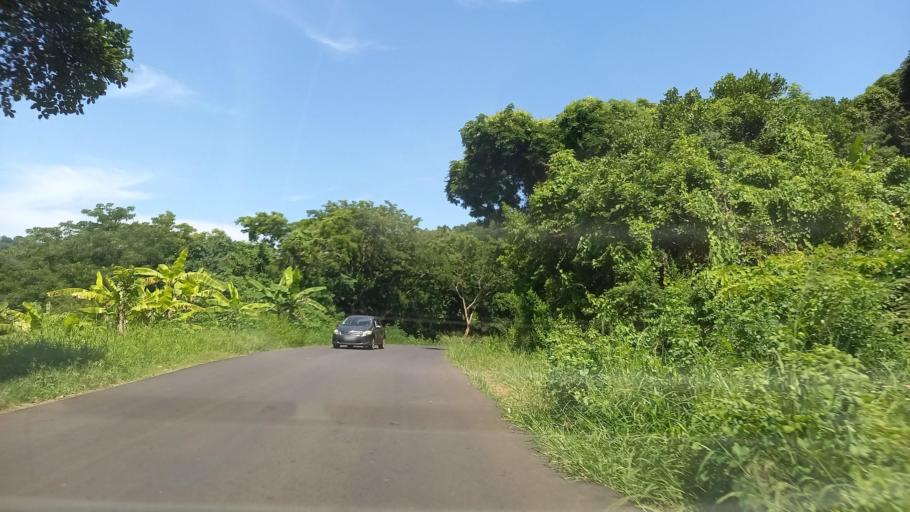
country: YT
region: M'Tsangamouji
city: M'Tsangamouji
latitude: -12.7504
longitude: 45.0643
